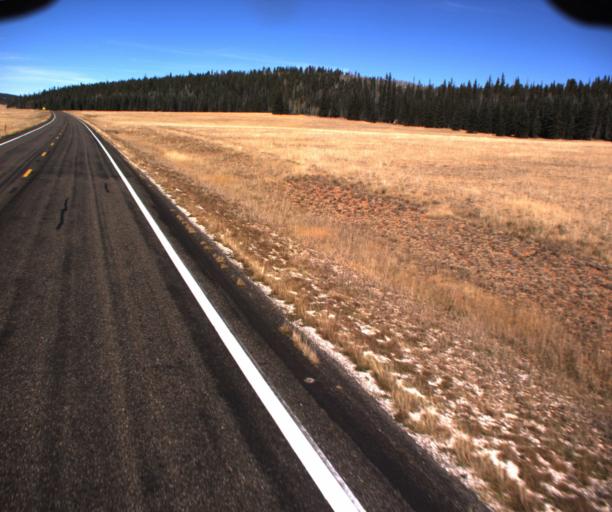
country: US
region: Arizona
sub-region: Coconino County
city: Grand Canyon
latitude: 36.3629
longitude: -112.1198
